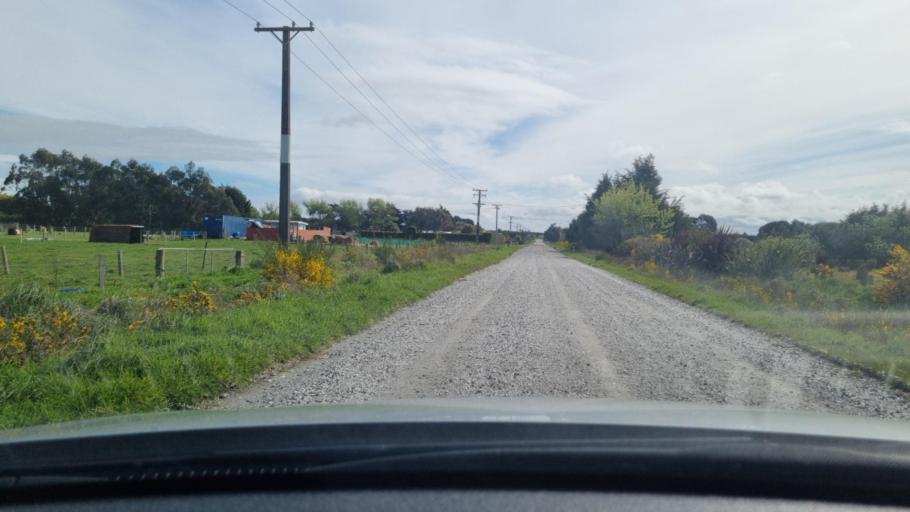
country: NZ
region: Southland
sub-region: Invercargill City
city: Invercargill
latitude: -46.4508
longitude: 168.3903
